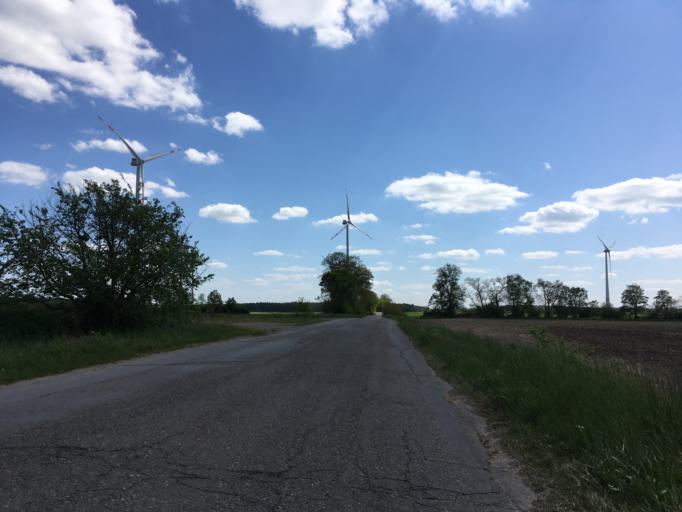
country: DE
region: Brandenburg
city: Rudnitz
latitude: 52.6884
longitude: 13.6708
